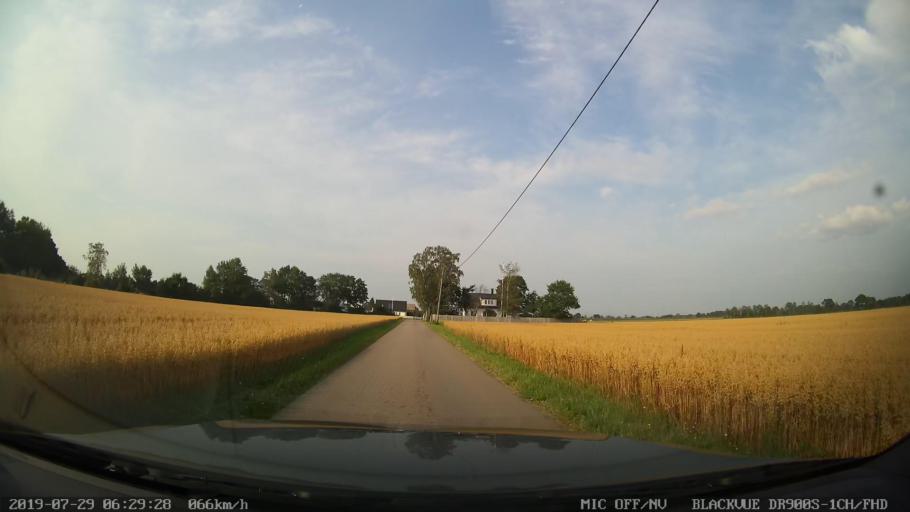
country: SE
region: Skane
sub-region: Helsingborg
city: Odakra
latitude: 56.1220
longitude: 12.7281
